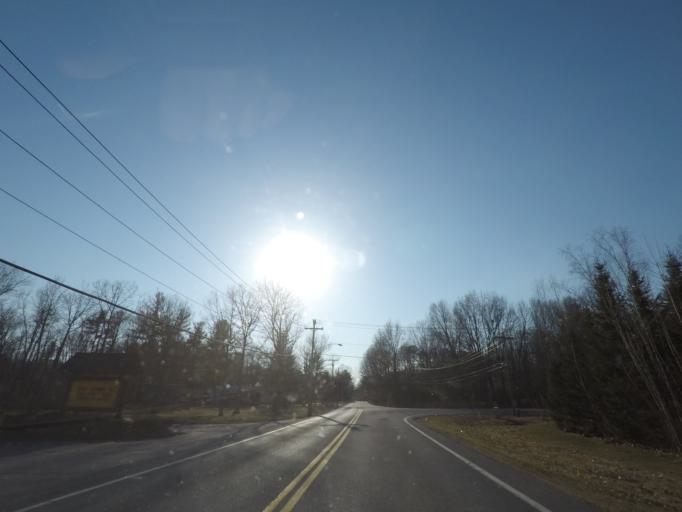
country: US
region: New York
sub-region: Schenectady County
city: Niskayuna
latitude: 42.8329
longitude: -73.7933
